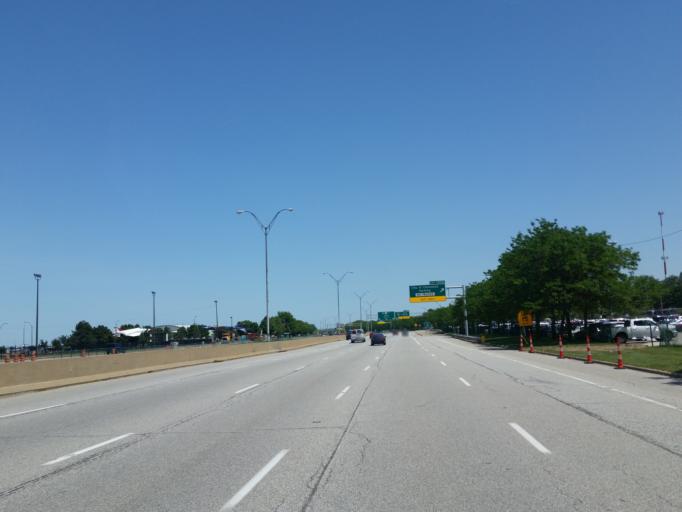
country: US
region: Ohio
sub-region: Cuyahoga County
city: Cleveland
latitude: 41.5093
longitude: -81.6899
